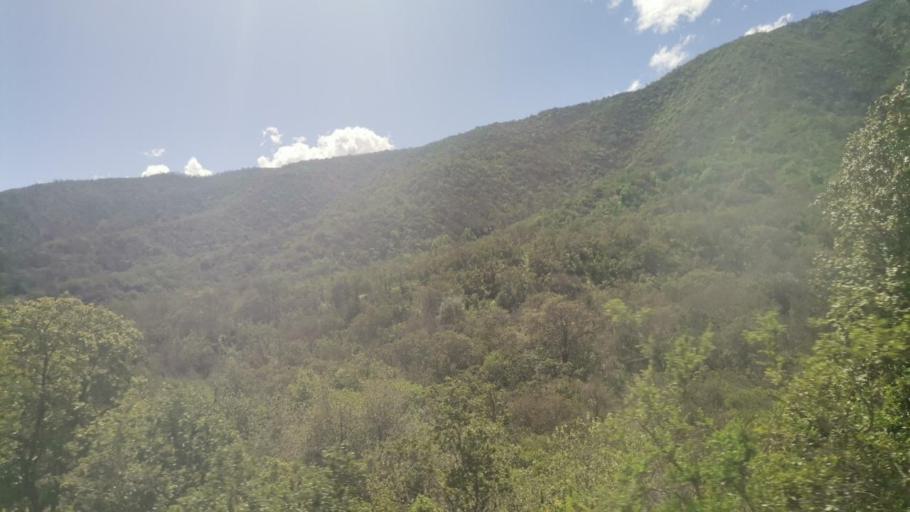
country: CL
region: Valparaiso
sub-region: Provincia de Marga Marga
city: Villa Alemana
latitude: -33.1931
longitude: -71.2812
